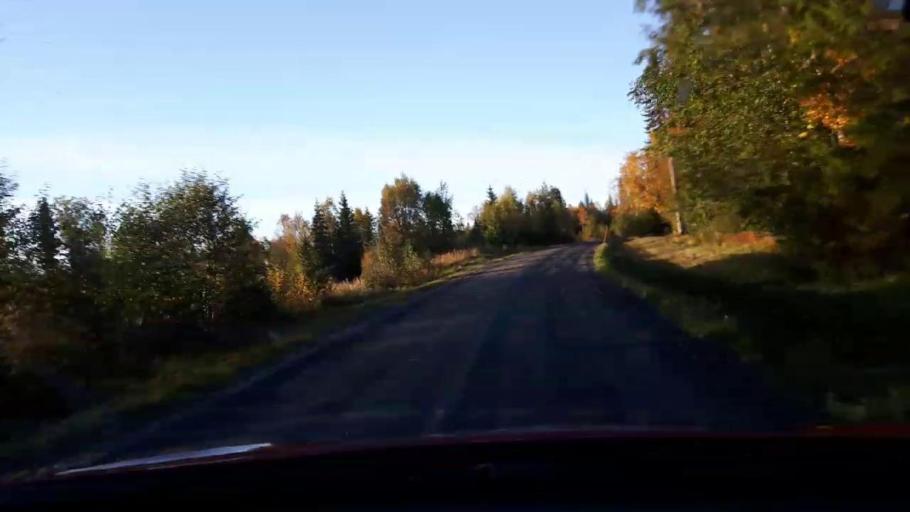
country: SE
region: Jaemtland
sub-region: Krokoms Kommun
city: Krokom
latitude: 63.4192
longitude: 14.6069
